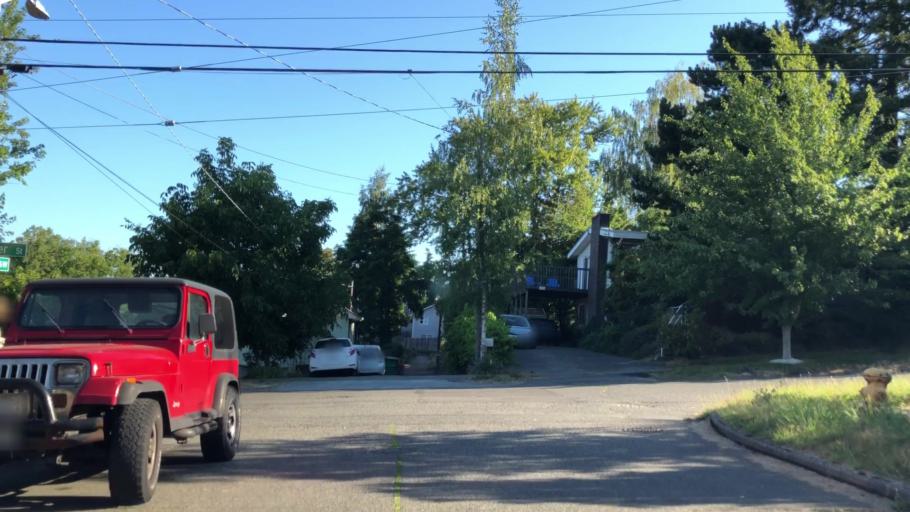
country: US
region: Washington
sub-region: King County
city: White Center
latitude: 47.5353
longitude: -122.3517
